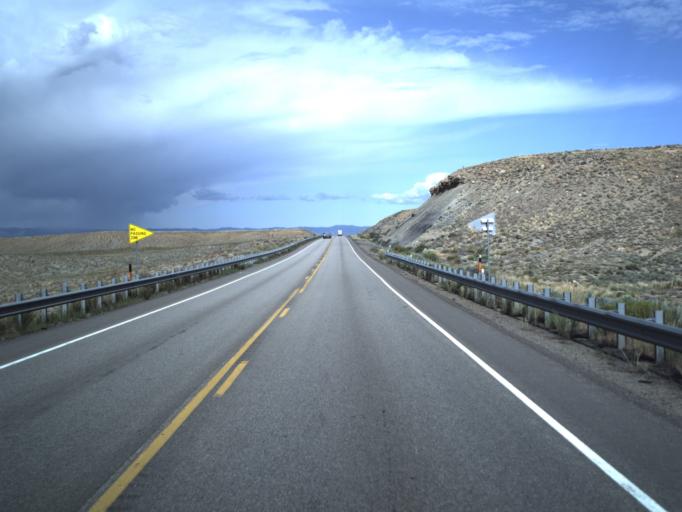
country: US
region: Utah
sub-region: Carbon County
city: East Carbon City
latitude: 39.5144
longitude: -110.5471
